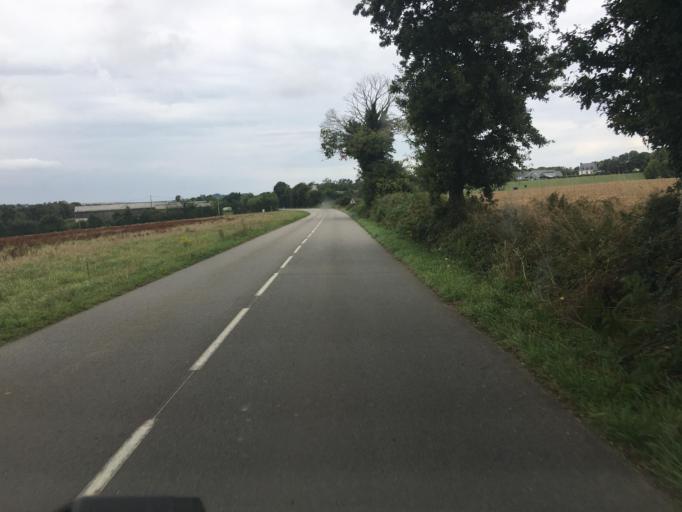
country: FR
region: Brittany
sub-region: Departement du Finistere
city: Plonevez-Porzay
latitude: 48.1279
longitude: -4.2283
